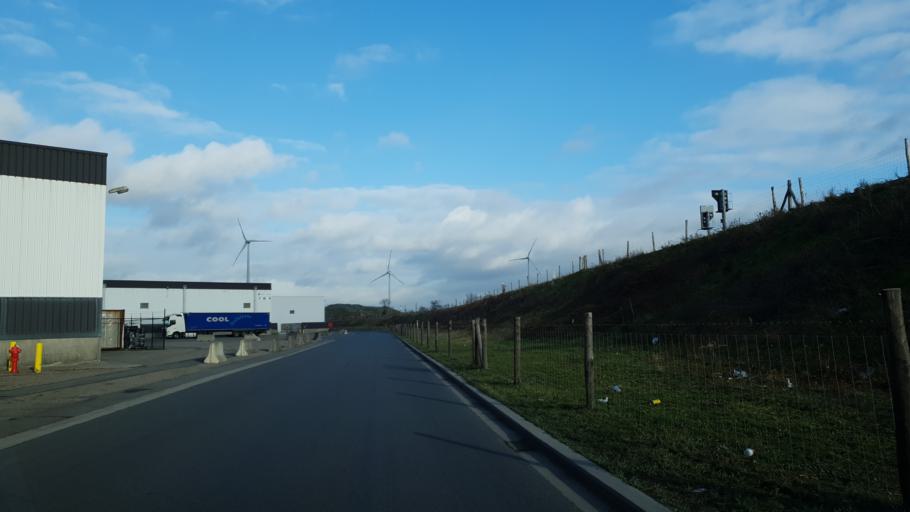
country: BE
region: Flanders
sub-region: Provincie Antwerpen
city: Stabroek
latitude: 51.3028
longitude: 4.3391
